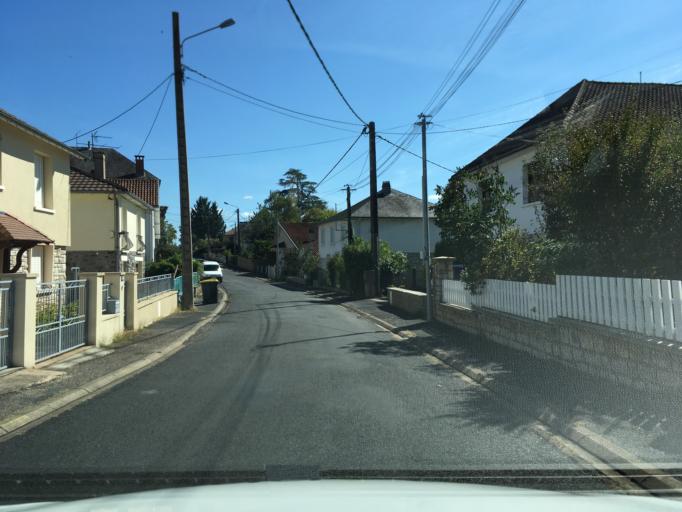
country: FR
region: Limousin
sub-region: Departement de la Correze
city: Brive-la-Gaillarde
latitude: 45.1706
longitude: 1.5208
